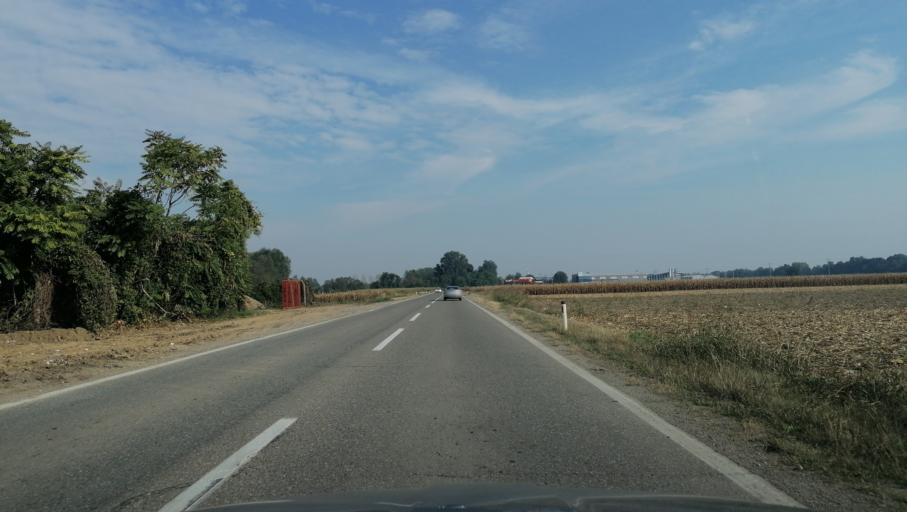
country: BA
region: Republika Srpska
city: Popovi
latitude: 44.7809
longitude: 19.3026
